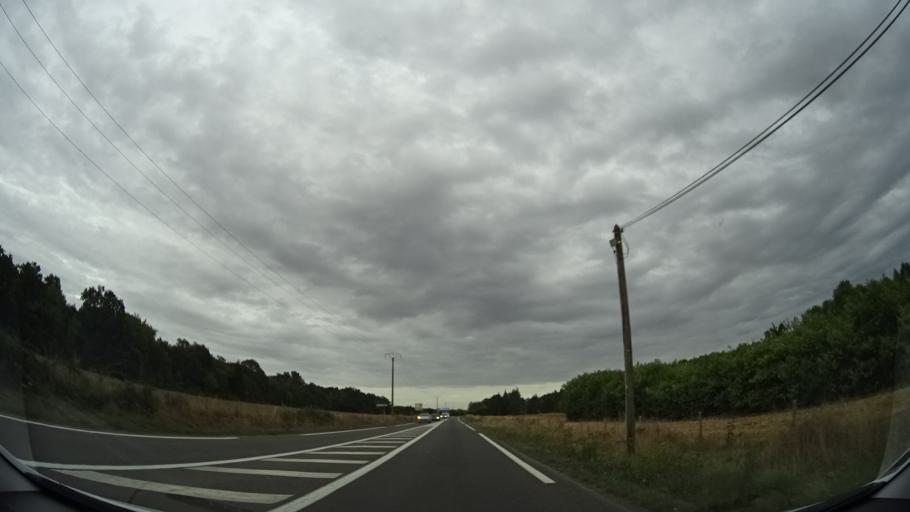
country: FR
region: Centre
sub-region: Departement du Loiret
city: Amilly
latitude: 47.9620
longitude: 2.7884
